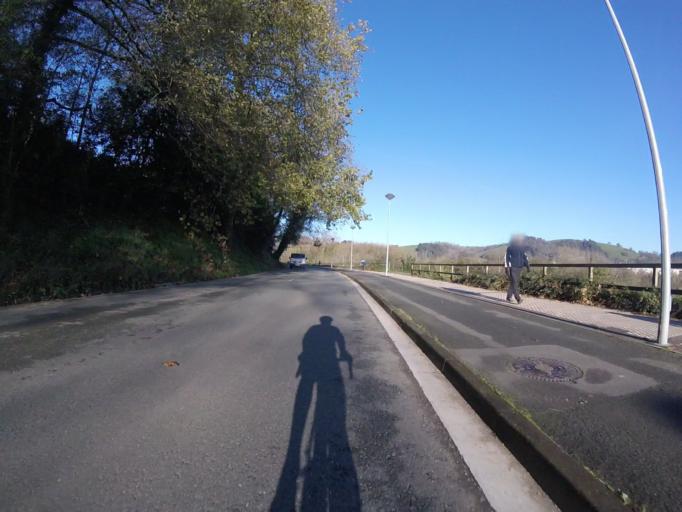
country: ES
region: Basque Country
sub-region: Provincia de Guipuzcoa
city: Lasarte
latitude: 43.2704
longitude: -2.0278
